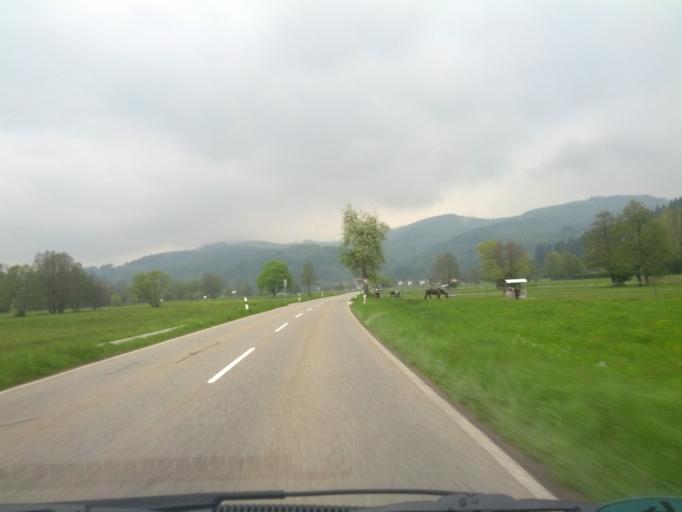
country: DE
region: Baden-Wuerttemberg
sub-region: Freiburg Region
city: Schopfheim
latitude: 47.6695
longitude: 7.8023
